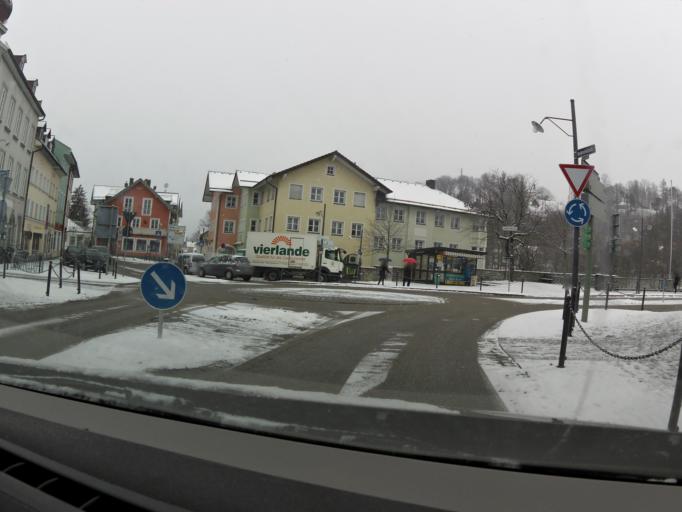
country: DE
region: Bavaria
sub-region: Upper Bavaria
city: Bad Toelz
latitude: 47.7600
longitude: 11.5560
